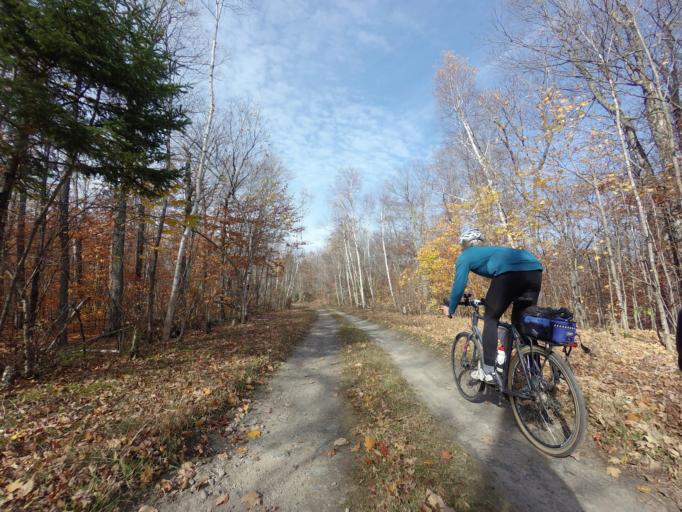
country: CA
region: Quebec
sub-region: Outaouais
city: Wakefield
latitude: 45.5250
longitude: -75.9281
